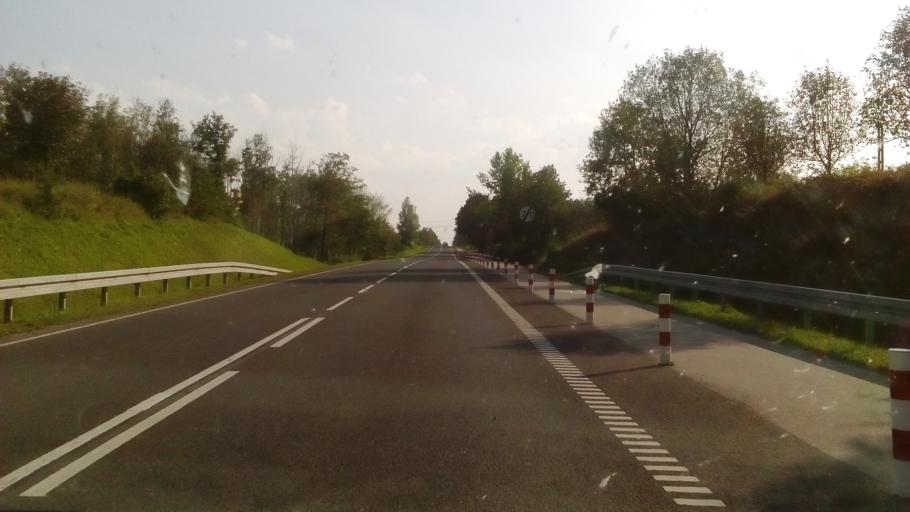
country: LT
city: Lazdijai
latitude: 54.1556
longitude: 23.4720
